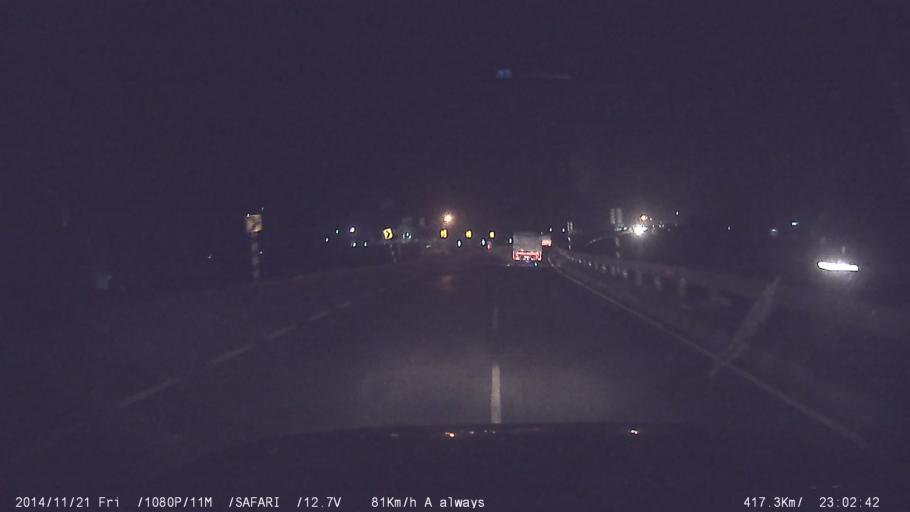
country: IN
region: Tamil Nadu
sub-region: Villupuram
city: Vikravandi
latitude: 12.0323
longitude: 79.5418
